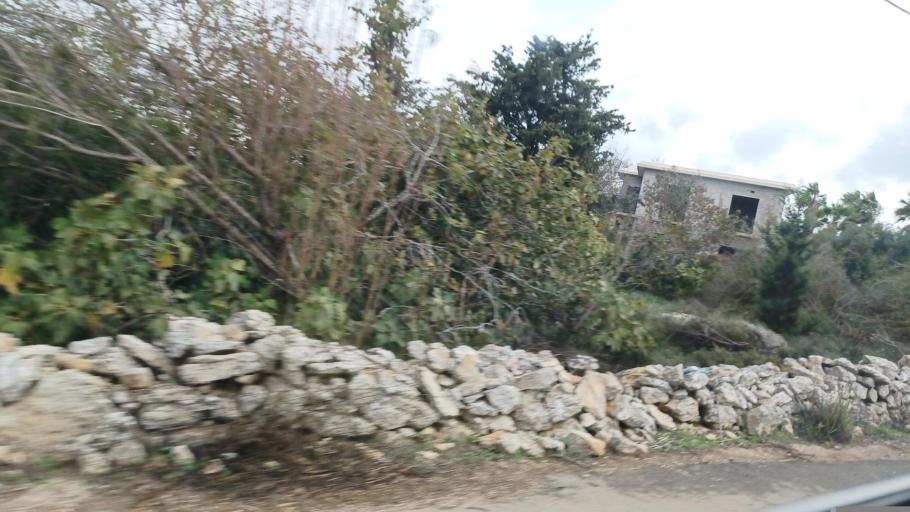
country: CY
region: Pafos
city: Pegeia
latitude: 34.9567
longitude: 32.4000
